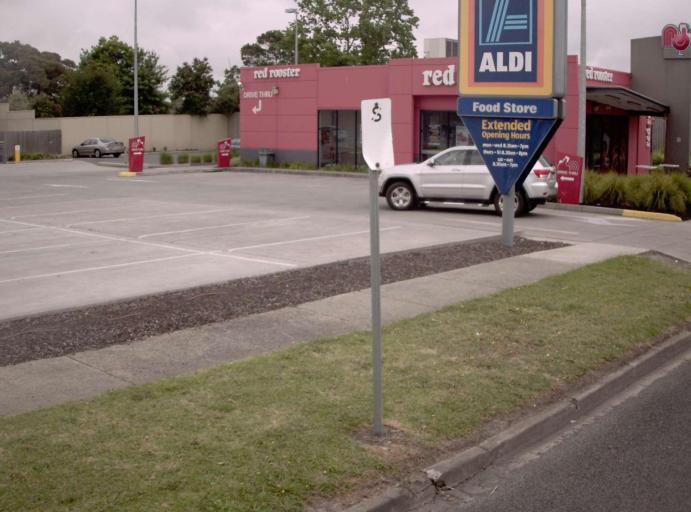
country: AU
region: Victoria
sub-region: Latrobe
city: Morwell
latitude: -38.2381
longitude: 146.4048
